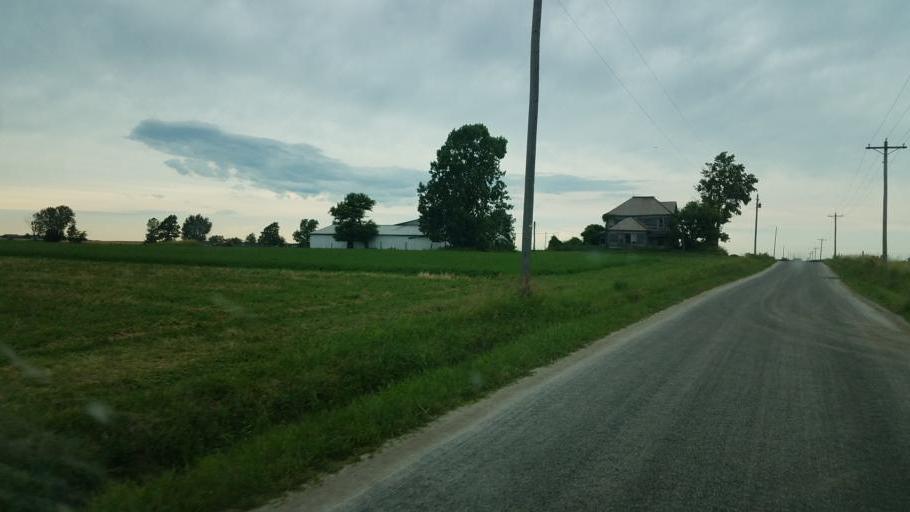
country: US
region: Ohio
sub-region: Ashland County
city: Ashland
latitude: 40.9442
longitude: -82.4073
